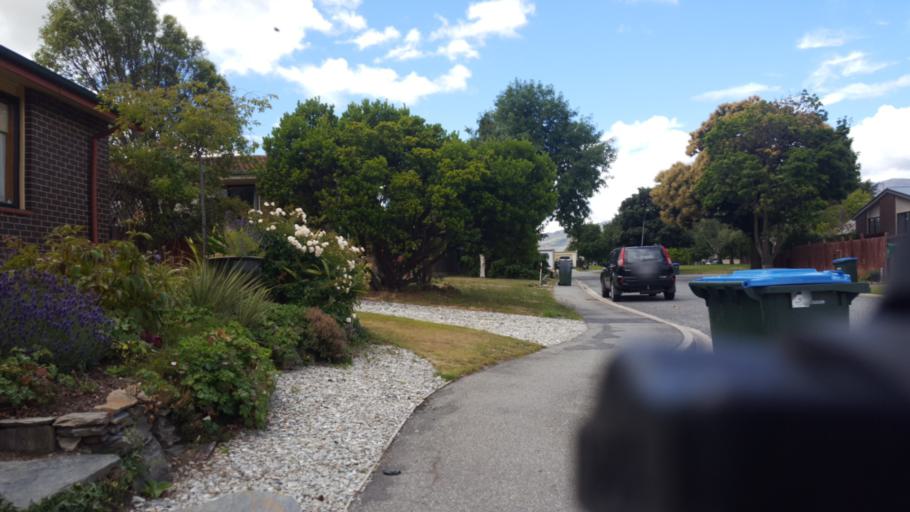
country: NZ
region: Otago
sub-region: Queenstown-Lakes District
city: Wanaka
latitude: -45.0406
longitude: 169.1827
